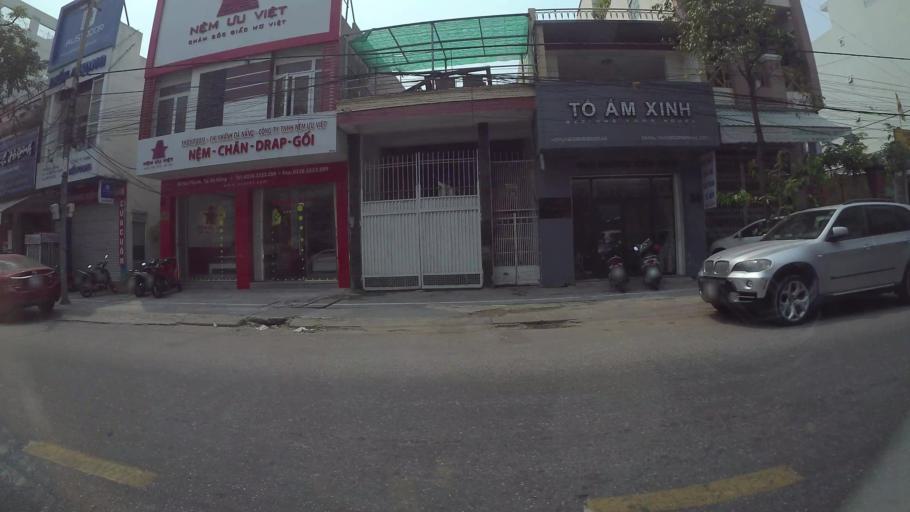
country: VN
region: Da Nang
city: Son Tra
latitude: 16.0517
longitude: 108.2204
